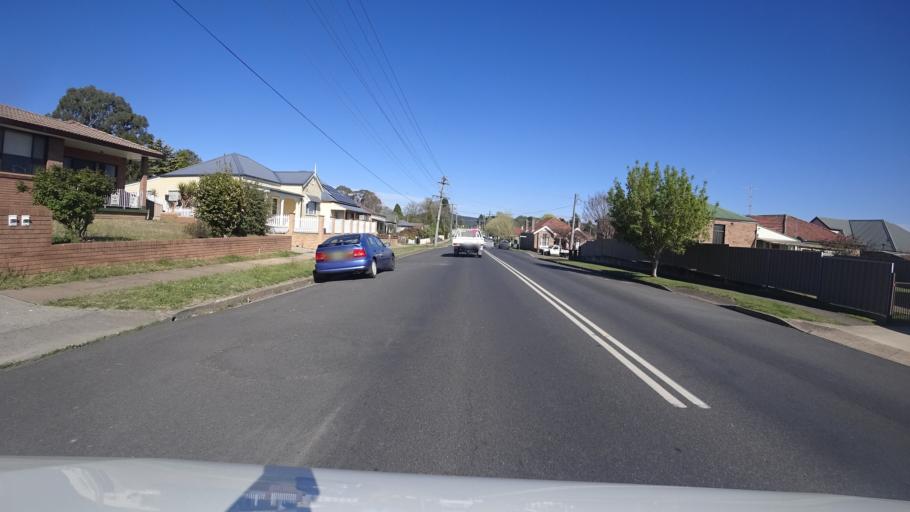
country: AU
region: New South Wales
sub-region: Lithgow
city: Lithgow
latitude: -33.4878
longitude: 150.1454
